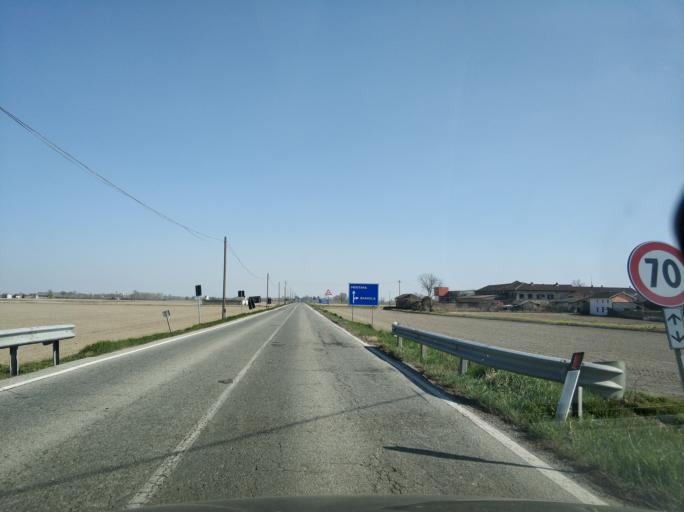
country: IT
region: Piedmont
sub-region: Provincia di Novara
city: Vinzaglio
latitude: 45.3146
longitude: 8.4974
